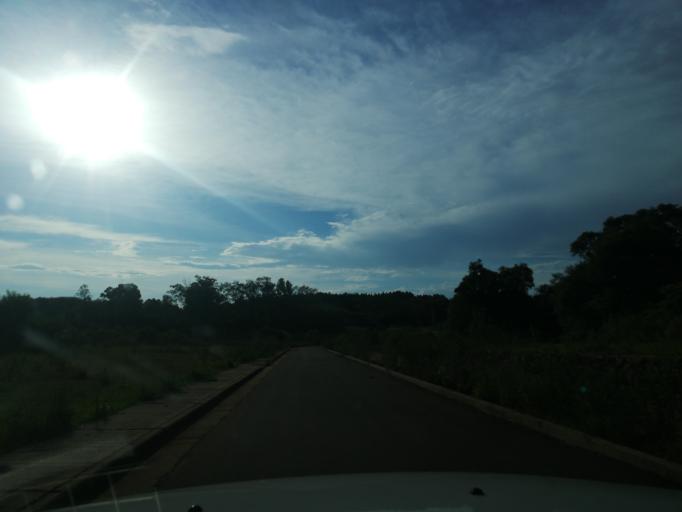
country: AR
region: Misiones
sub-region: Departamento de Candelaria
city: Candelaria
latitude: -27.4541
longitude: -55.7721
